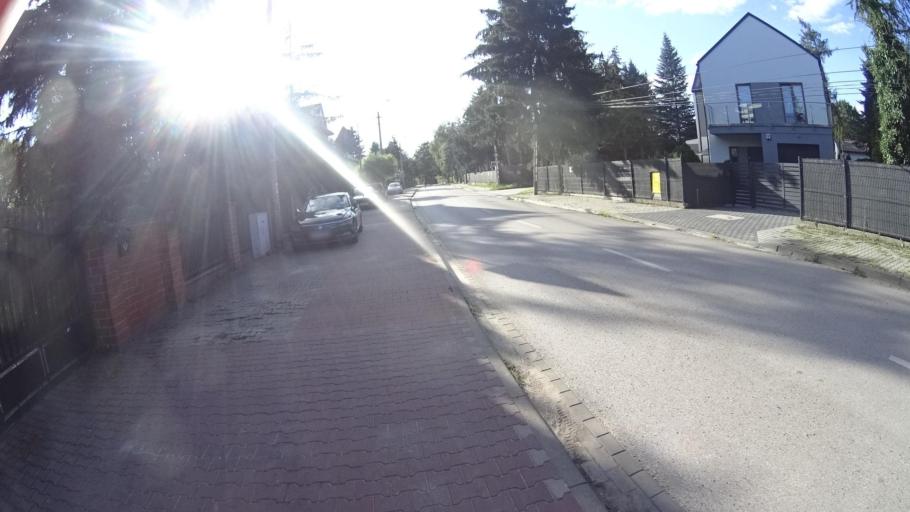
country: PL
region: Masovian Voivodeship
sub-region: Powiat piaseczynski
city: Piaseczno
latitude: 52.0655
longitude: 20.9942
